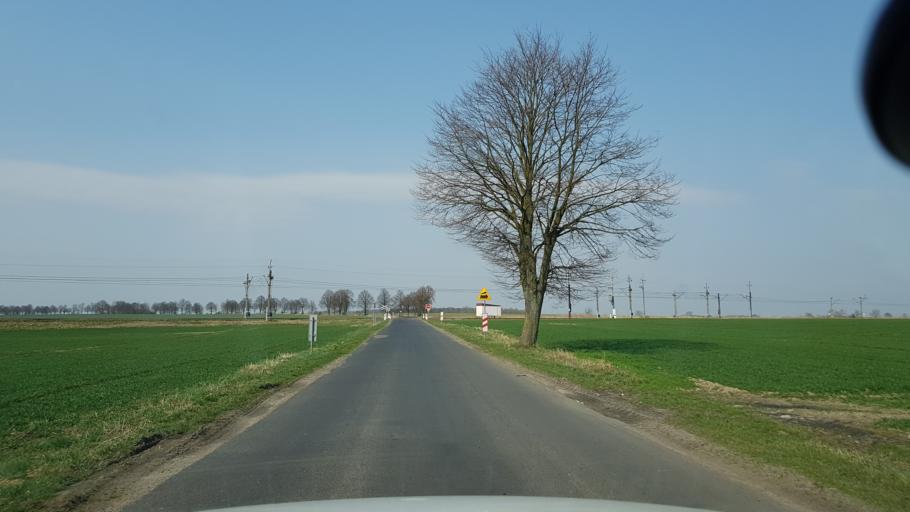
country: PL
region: West Pomeranian Voivodeship
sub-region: Powiat stargardzki
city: Stara Dabrowa
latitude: 53.3529
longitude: 15.1317
